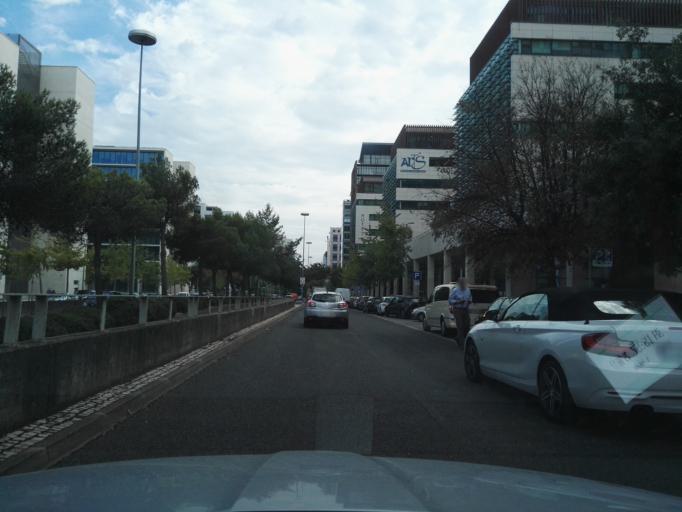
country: PT
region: Lisbon
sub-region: Loures
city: Moscavide
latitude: 38.7741
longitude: -9.0974
